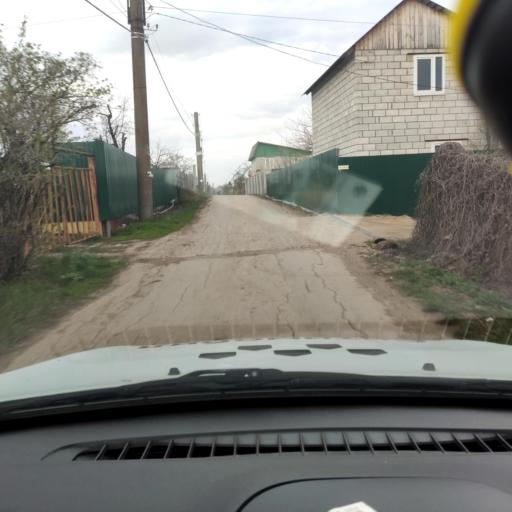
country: RU
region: Samara
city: Mezhdurechensk
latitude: 53.2446
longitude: 49.1507
